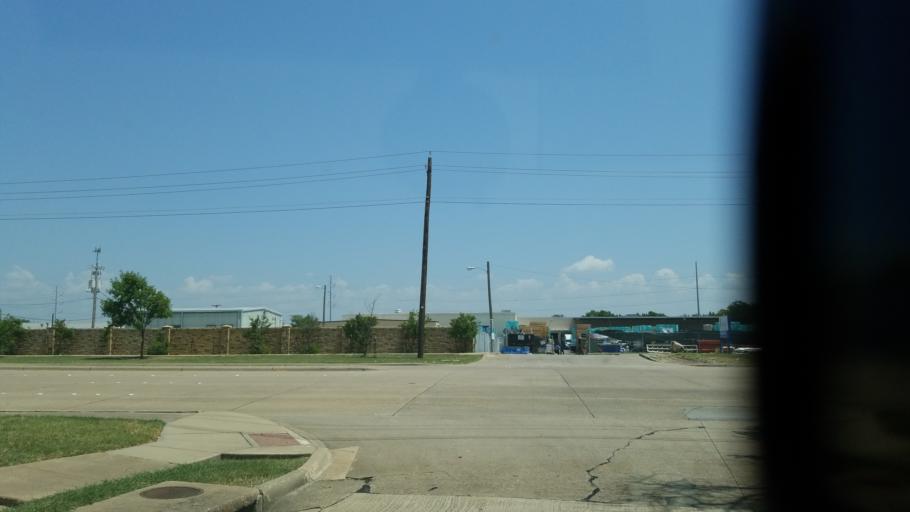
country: US
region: Texas
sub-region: Dallas County
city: Garland
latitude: 32.9283
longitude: -96.6309
